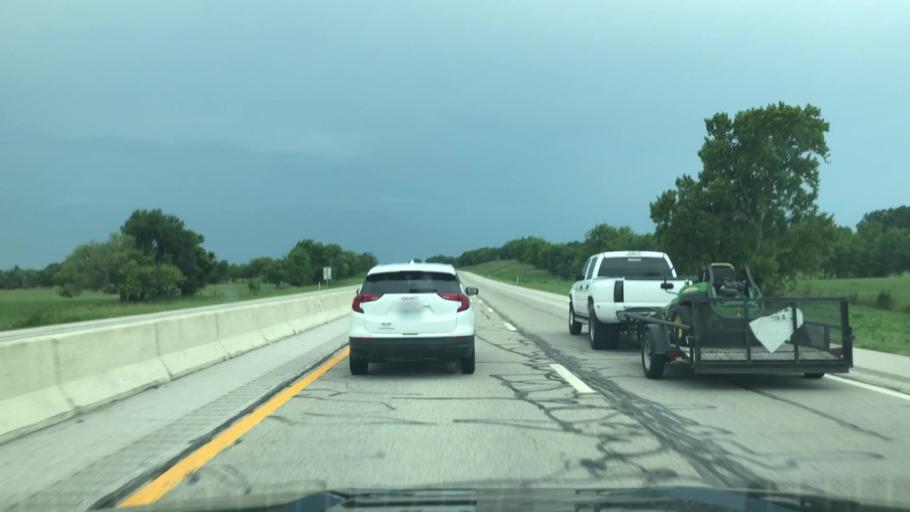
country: US
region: Oklahoma
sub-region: Rogers County
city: Chelsea
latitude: 36.4506
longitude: -95.3662
